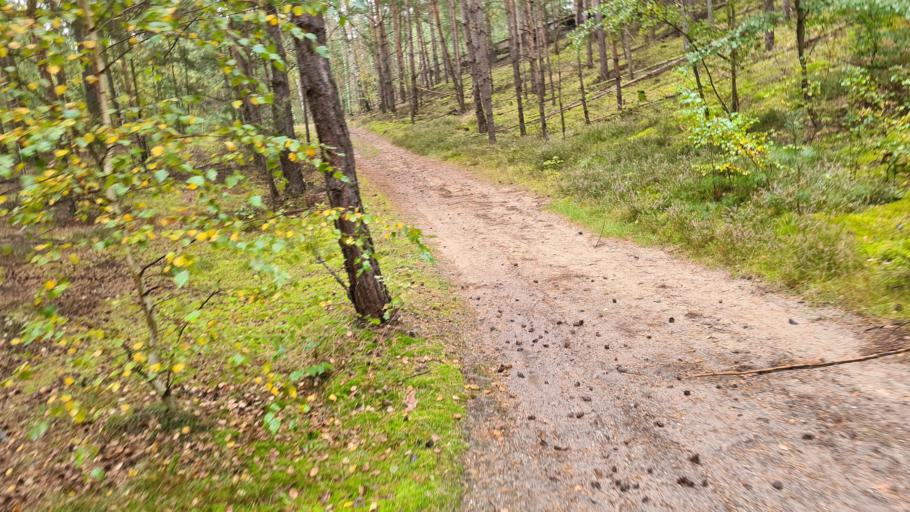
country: DE
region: Brandenburg
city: Schonewalde
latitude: 51.6300
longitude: 13.6202
